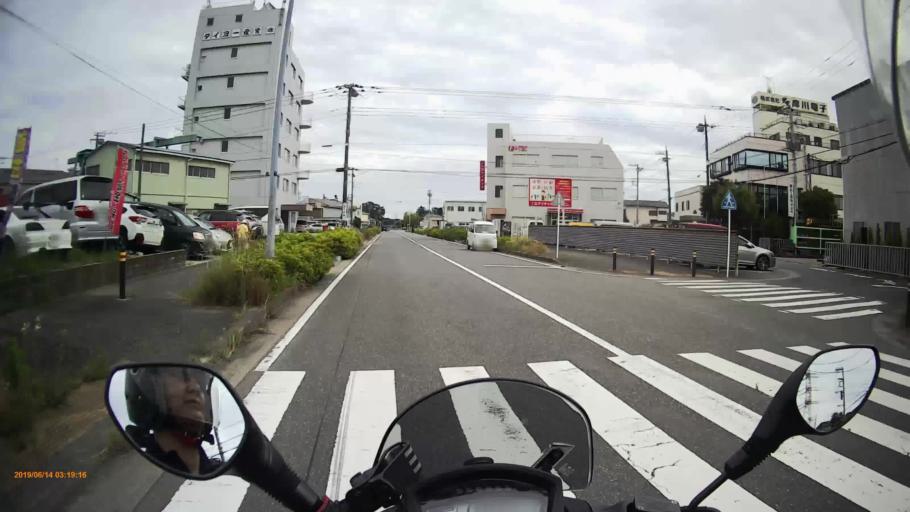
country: JP
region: Kanagawa
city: Minami-rinkan
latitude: 35.4169
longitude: 139.4533
